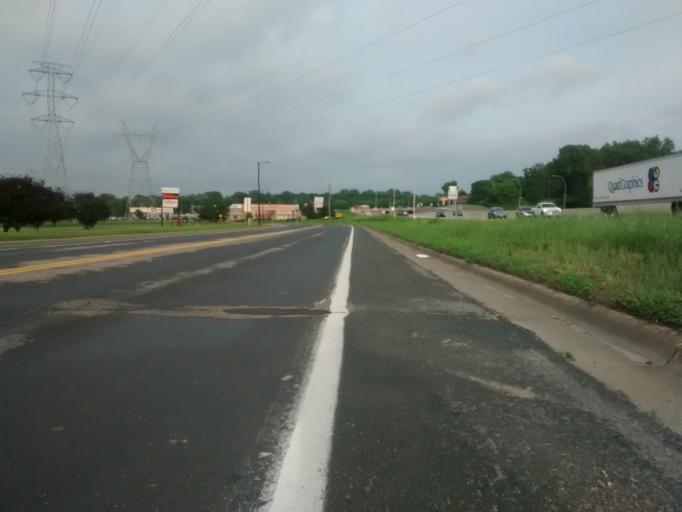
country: US
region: Minnesota
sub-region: Scott County
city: Savage
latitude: 44.7745
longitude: -93.3112
